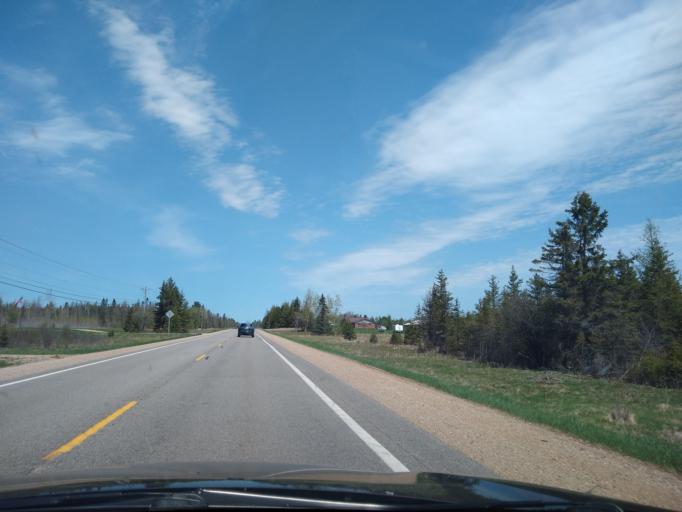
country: US
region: Michigan
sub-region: Delta County
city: Gladstone
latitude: 45.9454
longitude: -86.9720
